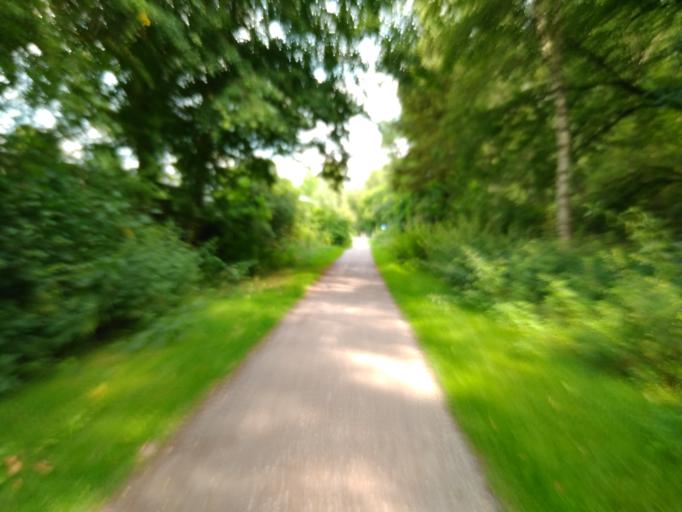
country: DE
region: North Rhine-Westphalia
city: Dorsten
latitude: 51.6741
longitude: 6.9437
